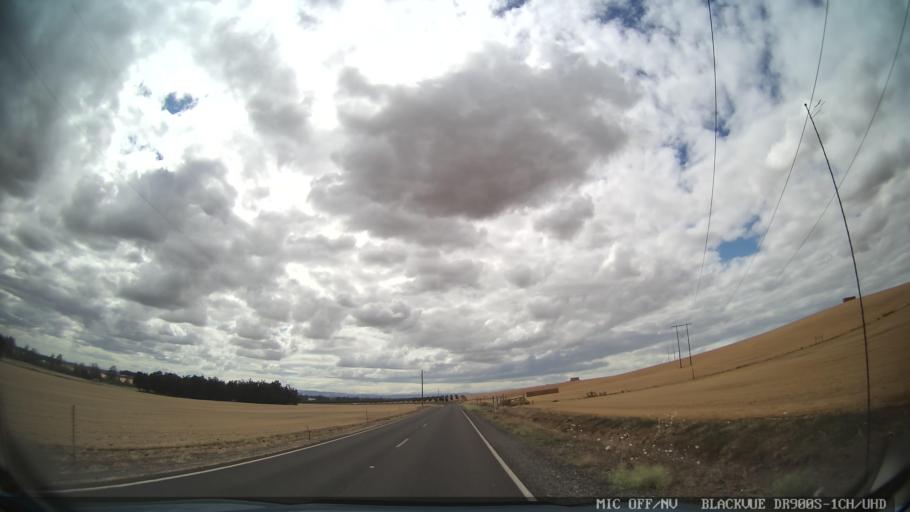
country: US
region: Oregon
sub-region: Marion County
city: Sublimity
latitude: 44.8478
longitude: -122.7478
